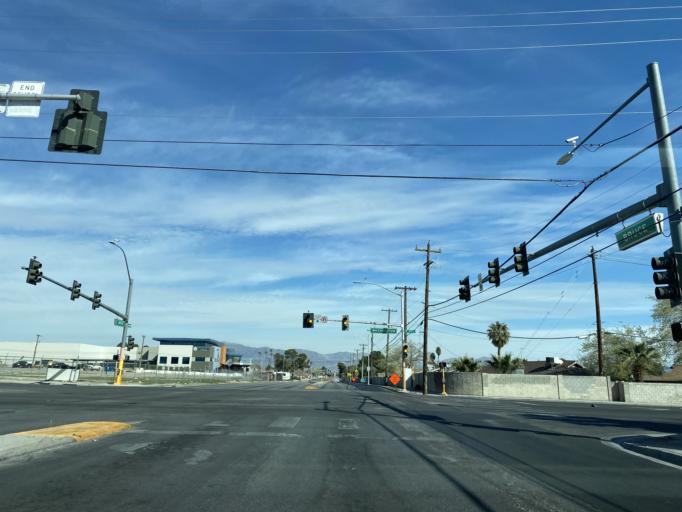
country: US
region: Nevada
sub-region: Clark County
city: Las Vegas
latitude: 36.1808
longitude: -115.1250
